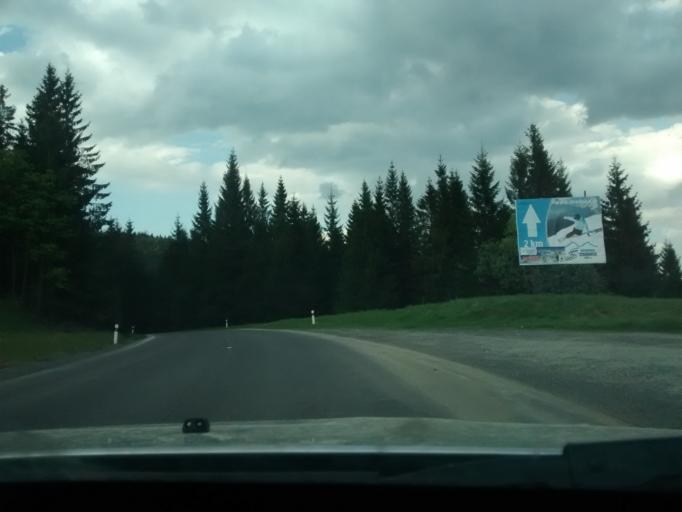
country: SK
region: Presovsky
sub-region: Okres Poprad
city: Zdiar
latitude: 49.2778
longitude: 20.2067
